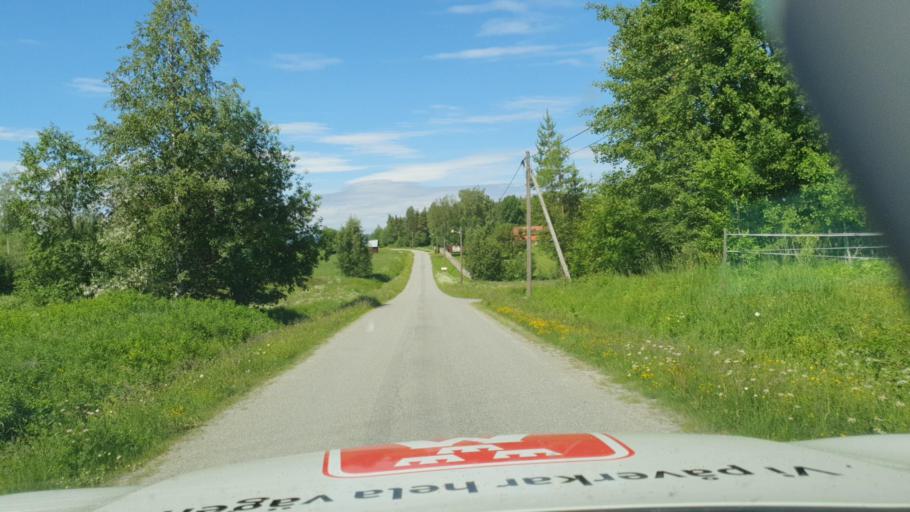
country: SE
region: Jaemtland
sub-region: Bergs Kommun
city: Hoverberg
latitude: 62.8457
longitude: 14.4293
